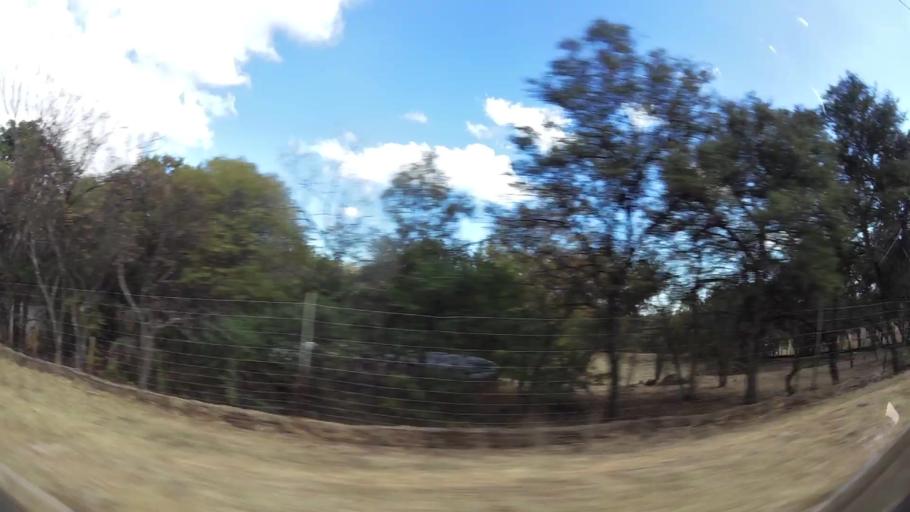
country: ZA
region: Gauteng
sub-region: West Rand District Municipality
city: Muldersdriseloop
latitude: -26.0868
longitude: 27.8536
